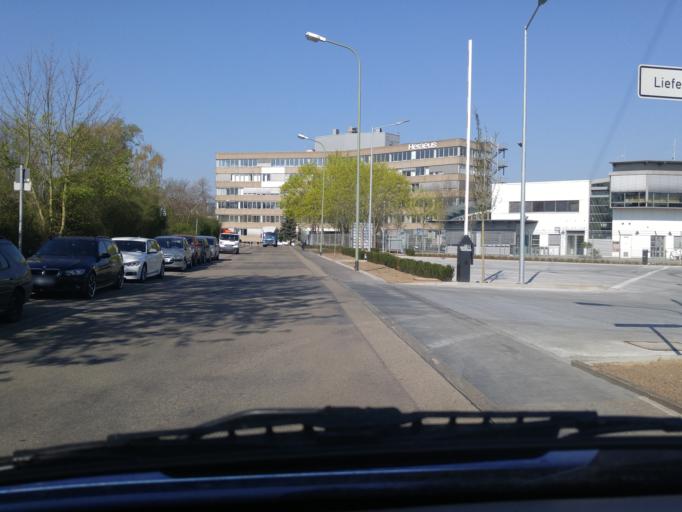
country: DE
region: Hesse
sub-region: Regierungsbezirk Darmstadt
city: Hanau am Main
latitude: 50.1310
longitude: 8.9368
